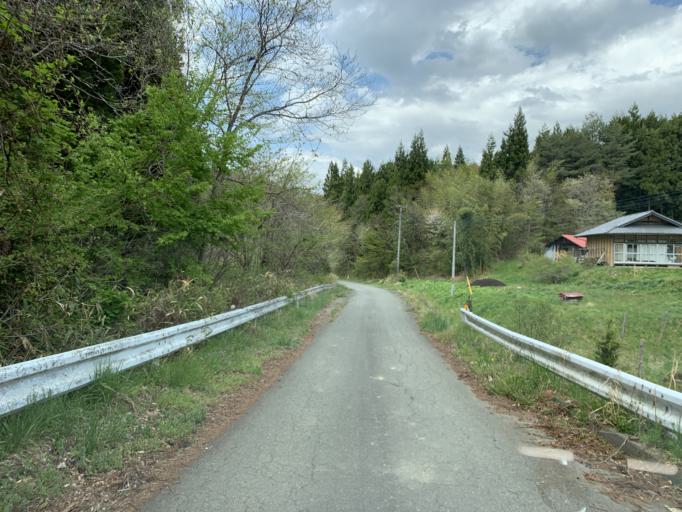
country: JP
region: Iwate
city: Ichinoseki
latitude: 38.7836
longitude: 141.4329
